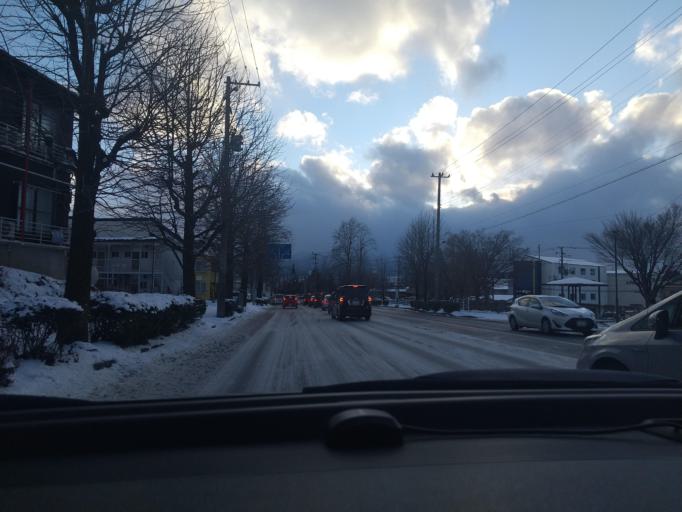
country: JP
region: Iwate
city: Morioka-shi
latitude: 39.7246
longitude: 141.1365
